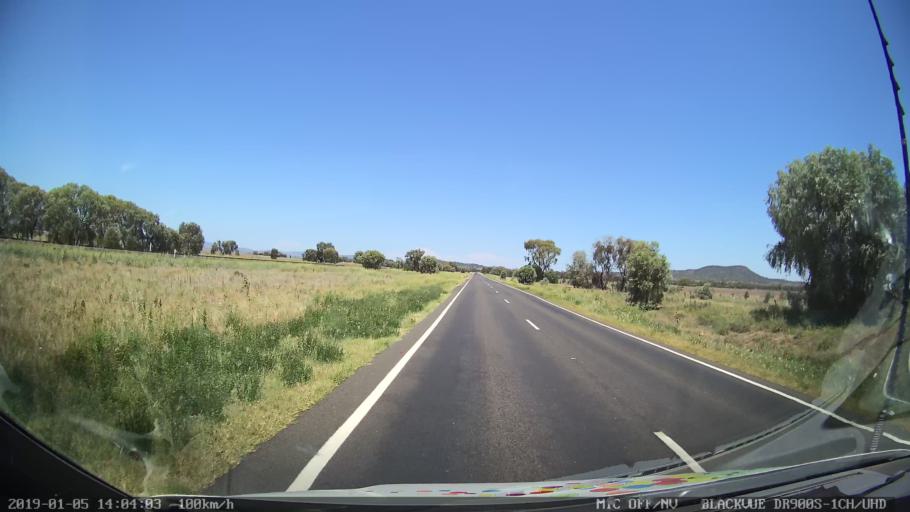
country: AU
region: New South Wales
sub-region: Gunnedah
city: Gunnedah
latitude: -31.1961
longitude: 150.3588
